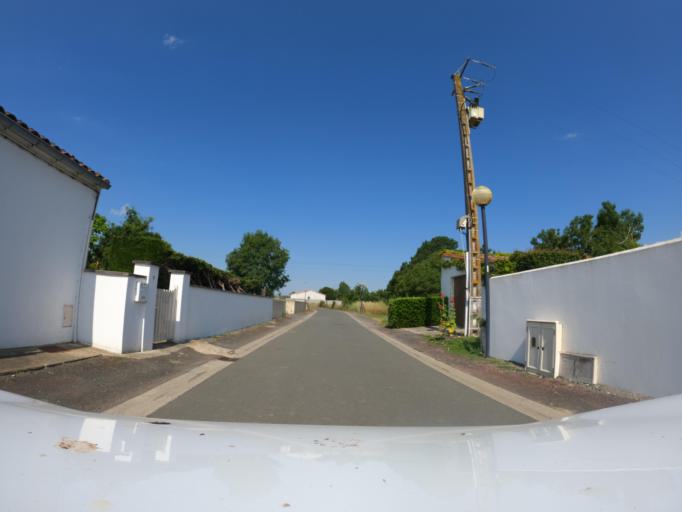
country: FR
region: Pays de la Loire
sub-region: Departement de la Vendee
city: Champagne-les-Marais
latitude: 46.3804
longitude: -1.1095
